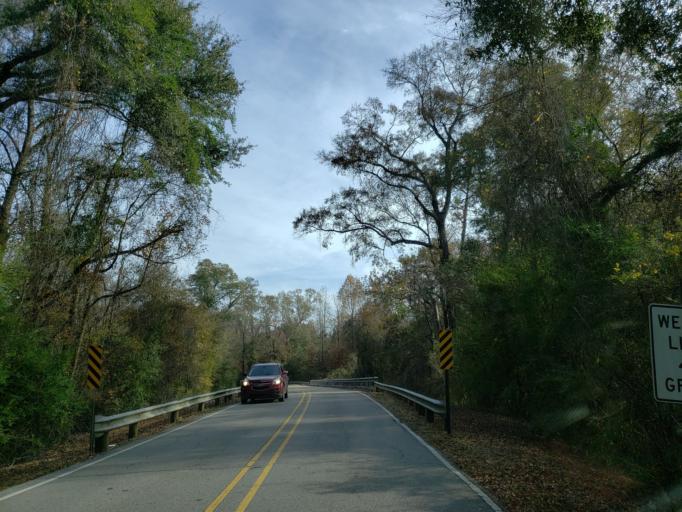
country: US
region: Mississippi
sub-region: Forrest County
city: Rawls Springs
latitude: 31.3878
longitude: -89.3785
